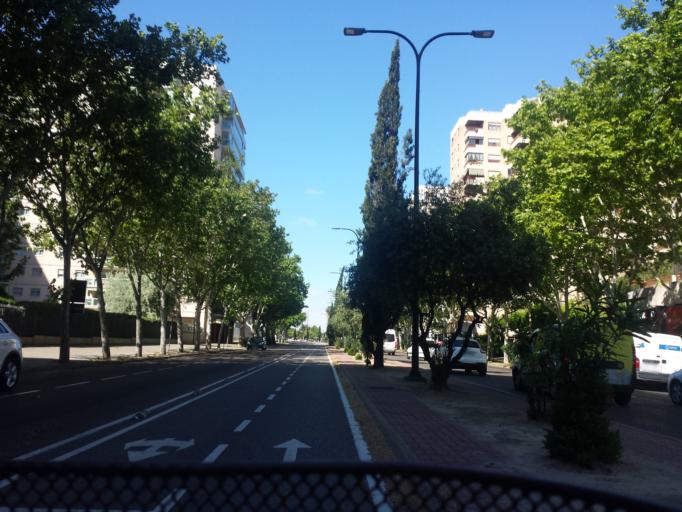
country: ES
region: Aragon
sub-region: Provincia de Zaragoza
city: Delicias
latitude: 41.6414
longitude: -0.9115
